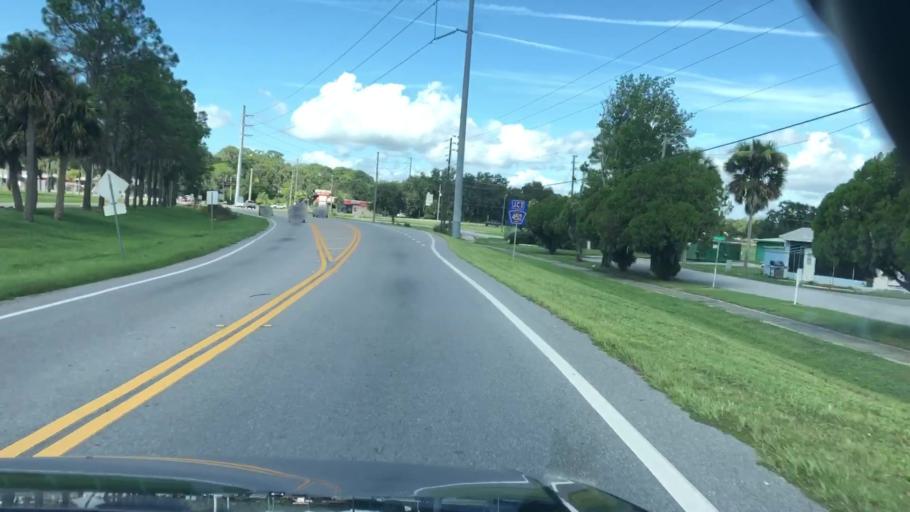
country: US
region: Florida
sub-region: Lake County
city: Eustis
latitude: 28.8752
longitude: -81.6966
